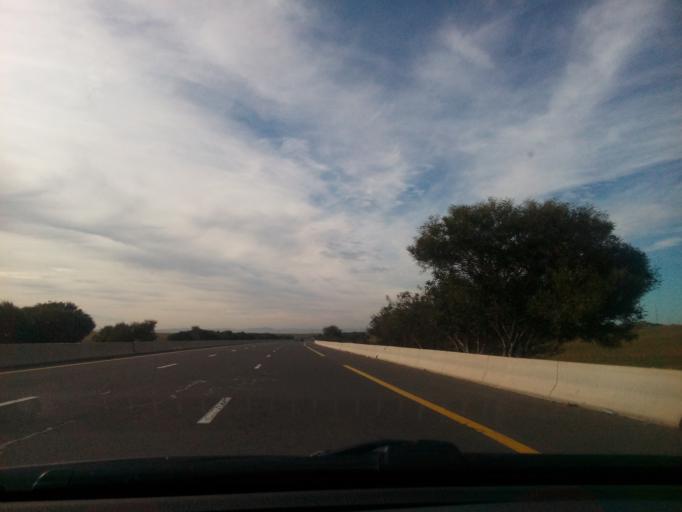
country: DZ
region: Sidi Bel Abbes
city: Sidi Bel Abbes
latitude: 35.2009
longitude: -0.6920
